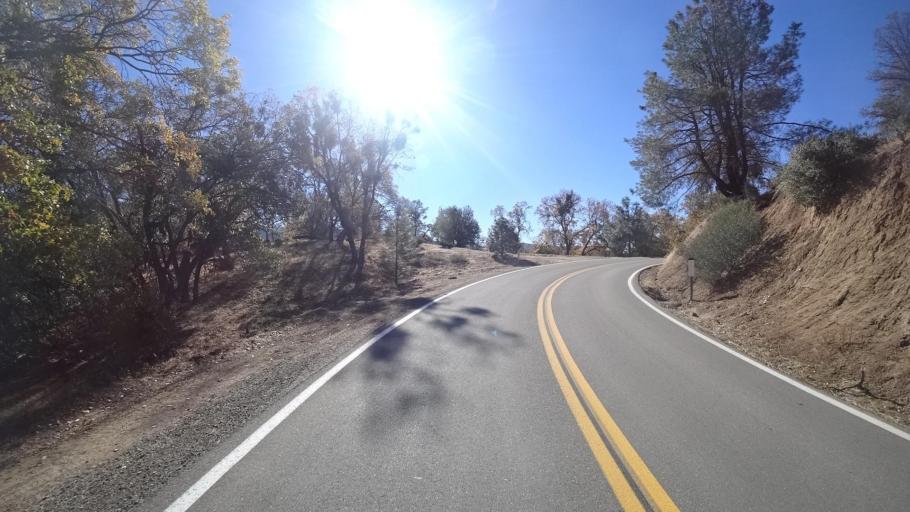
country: US
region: California
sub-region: Kern County
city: Alta Sierra
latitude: 35.7430
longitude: -118.6033
